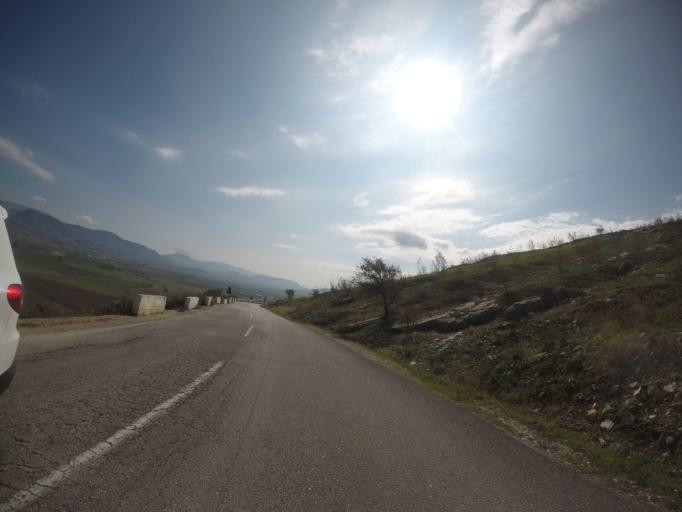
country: AL
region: Gjirokaster
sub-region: Rrethi i Gjirokastres
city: Libohove
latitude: 39.9466
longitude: 20.2551
